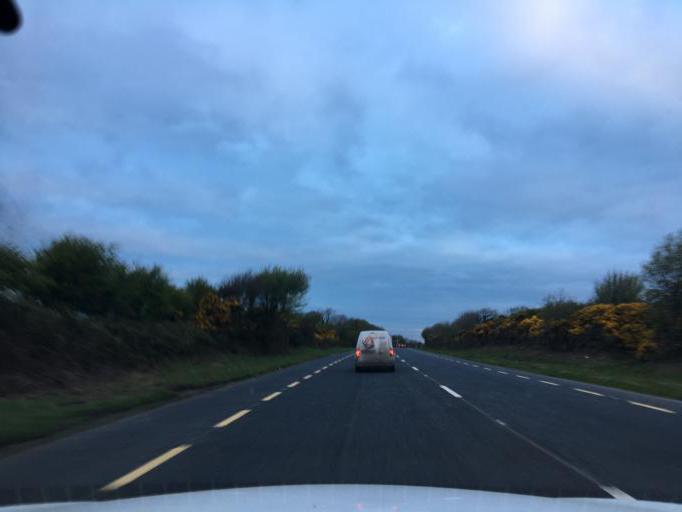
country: IE
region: Leinster
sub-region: Loch Garman
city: Loch Garman
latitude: 52.3137
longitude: -6.4904
